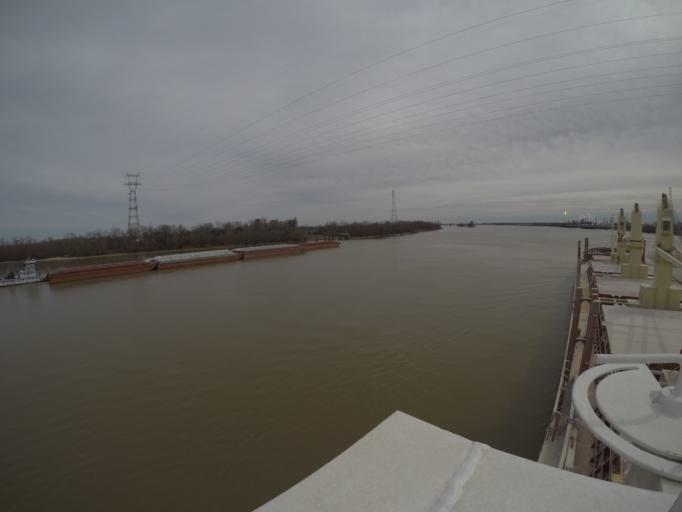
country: US
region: Louisiana
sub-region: Saint Charles Parish
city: Montz
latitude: 30.0011
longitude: -90.4707
